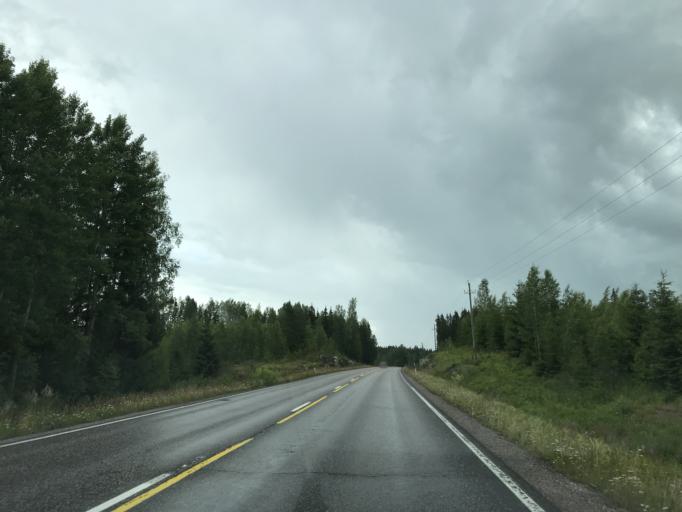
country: FI
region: Paijanne Tavastia
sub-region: Lahti
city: Orimattila
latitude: 60.7887
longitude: 25.6354
